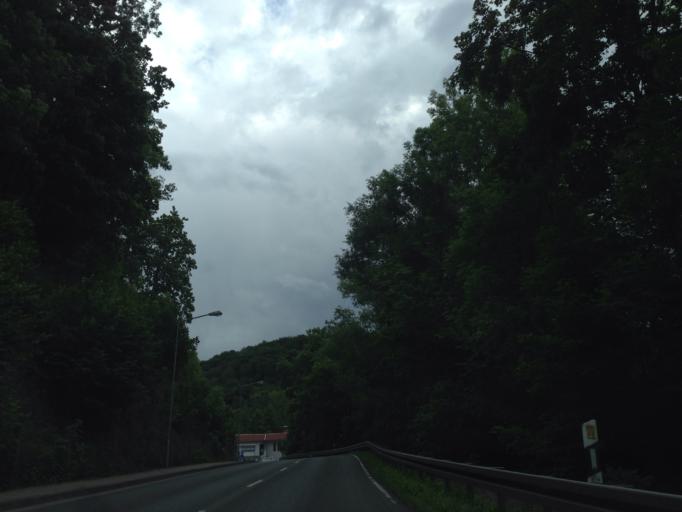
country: DE
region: Thuringia
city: Rudolstadt
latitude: 50.7313
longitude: 11.3339
